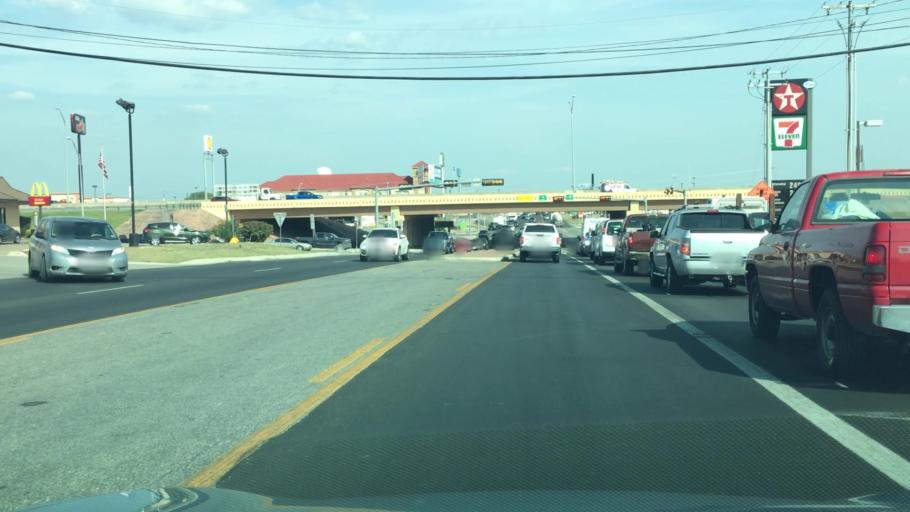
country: US
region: Texas
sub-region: Comal County
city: New Braunfels
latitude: 29.7012
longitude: -98.0950
